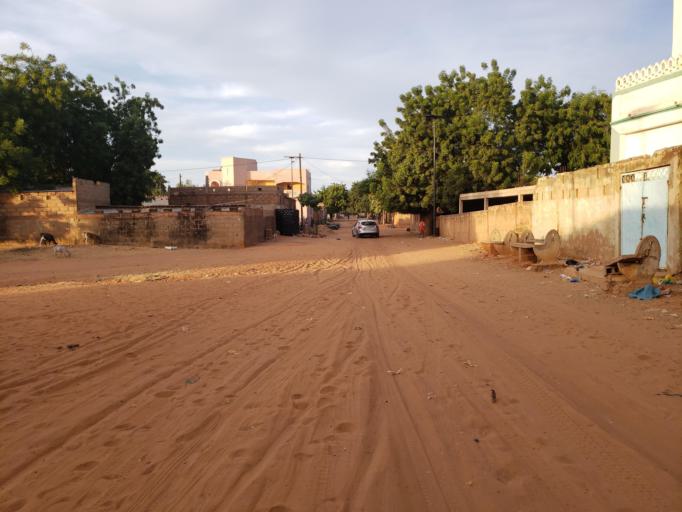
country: SN
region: Louga
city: Ndibene Dahra
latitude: 15.3936
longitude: -15.1132
